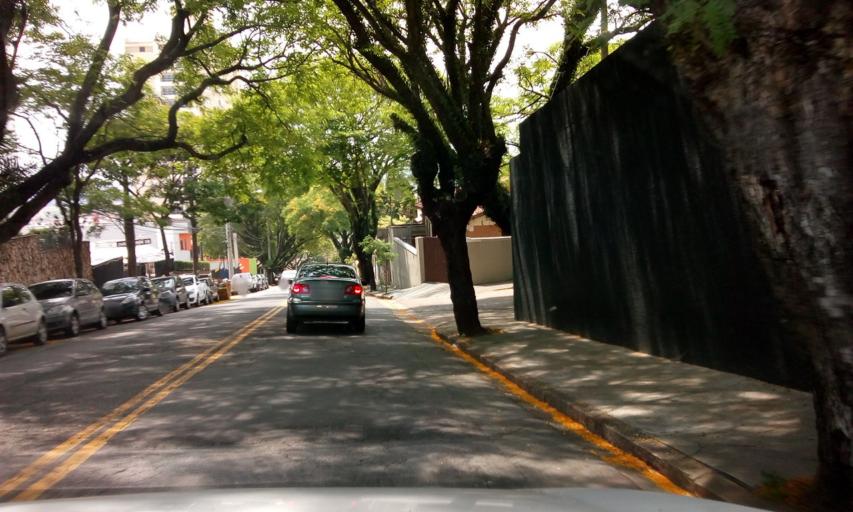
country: BR
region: Sao Paulo
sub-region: Jundiai
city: Jundiai
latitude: -23.2033
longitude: -46.8892
